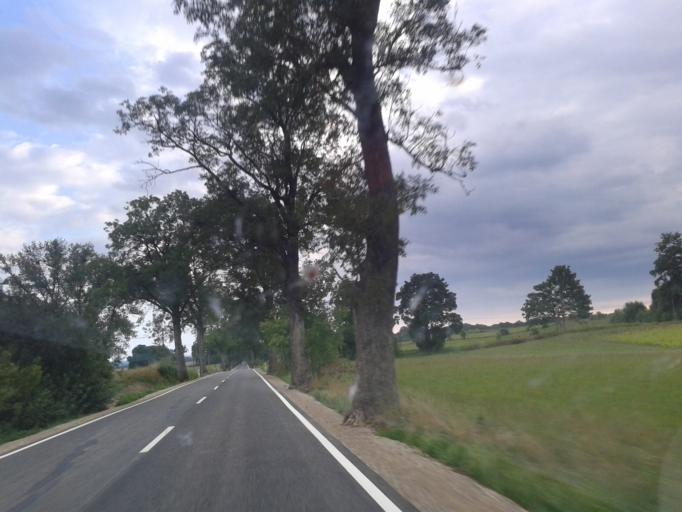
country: PL
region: West Pomeranian Voivodeship
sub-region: Powiat szczecinecki
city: Grzmiaca
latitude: 53.8656
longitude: 16.4824
